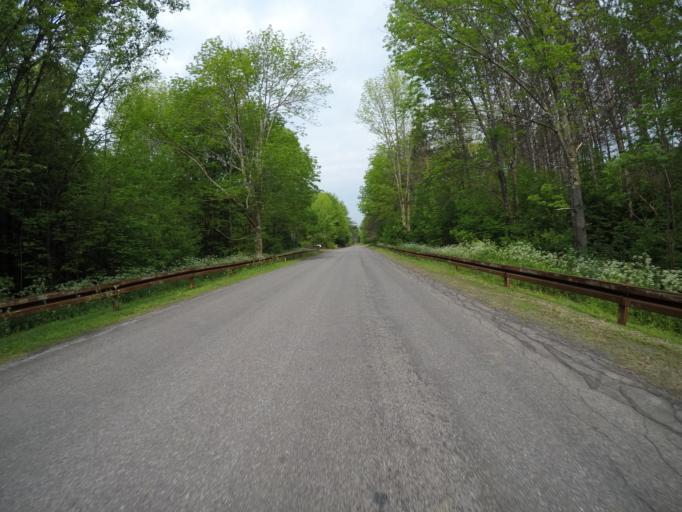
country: US
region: New York
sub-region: Sullivan County
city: Livingston Manor
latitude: 42.0821
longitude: -74.7913
